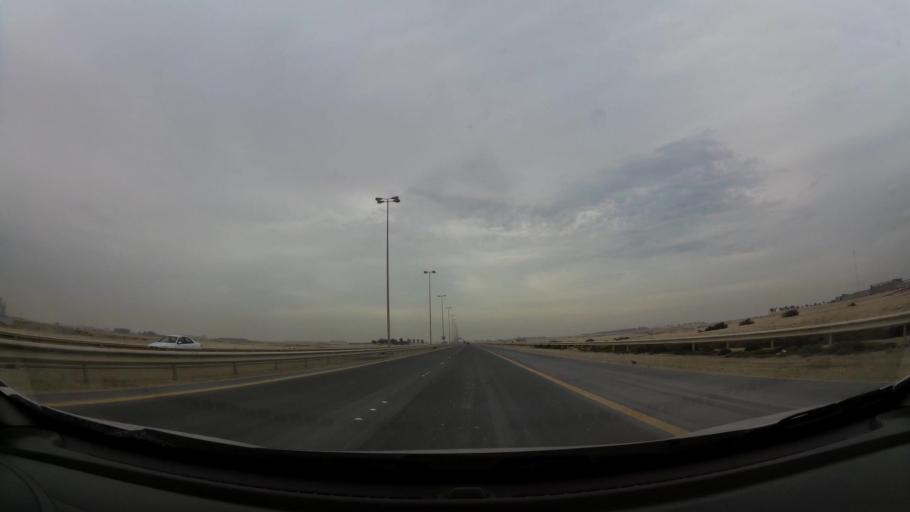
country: BH
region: Central Governorate
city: Dar Kulayb
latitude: 26.0266
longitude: 50.6078
